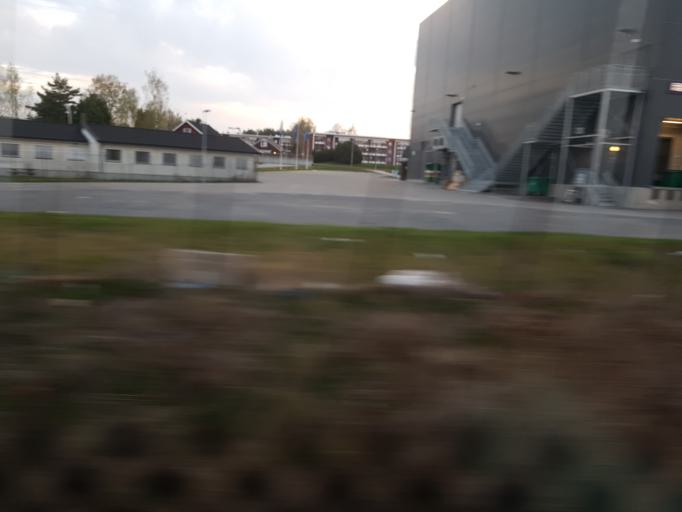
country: NO
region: Hedmark
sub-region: Hamar
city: Hamar
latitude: 60.8014
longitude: 11.0341
